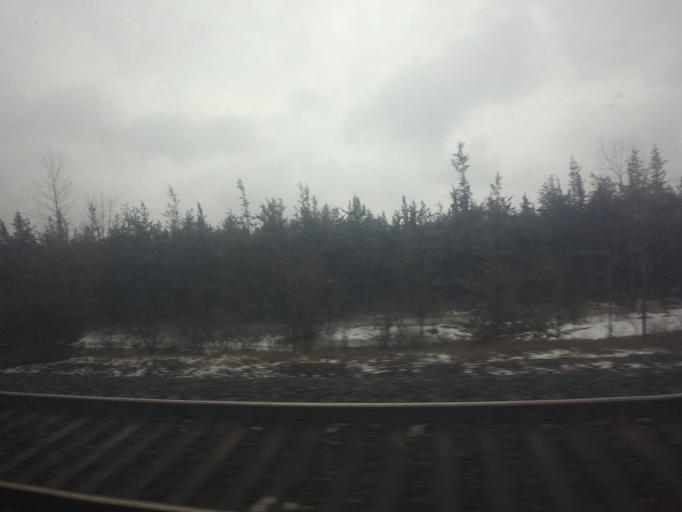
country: CA
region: Ontario
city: Belleville
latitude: 44.2029
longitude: -77.2432
